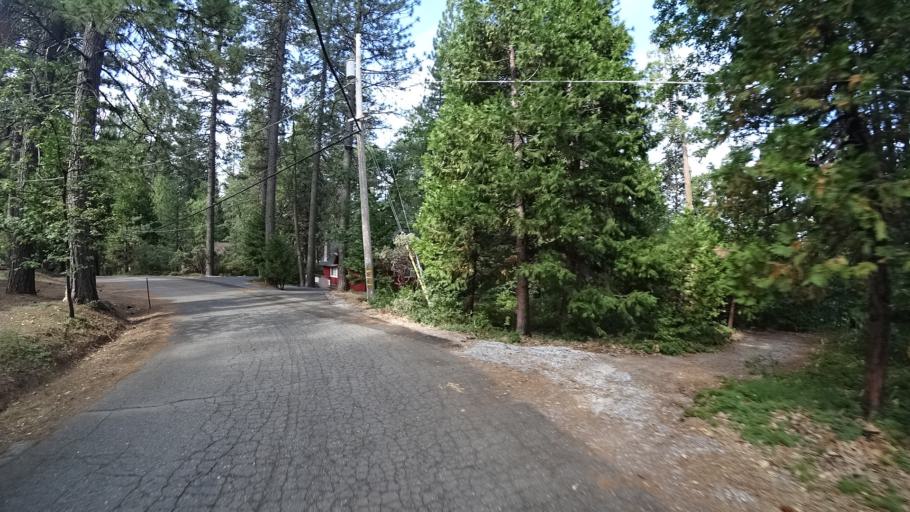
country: US
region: California
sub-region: Calaveras County
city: Arnold
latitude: 38.2636
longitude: -120.3349
